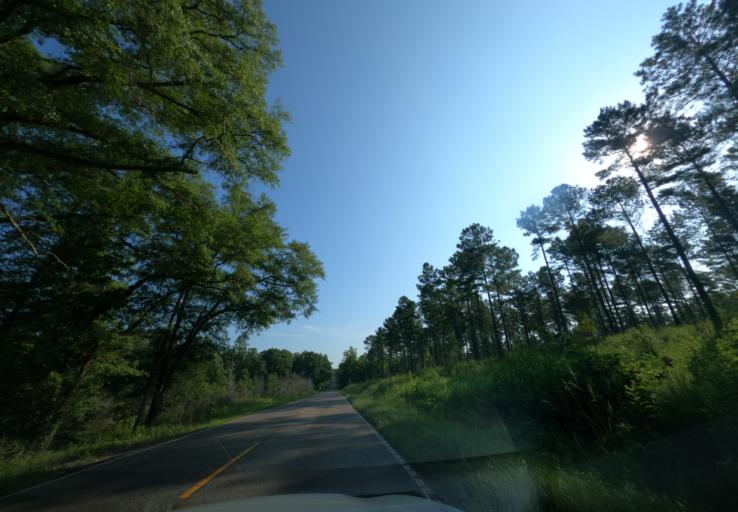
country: US
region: South Carolina
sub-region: Edgefield County
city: Edgefield
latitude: 33.7493
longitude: -81.9587
